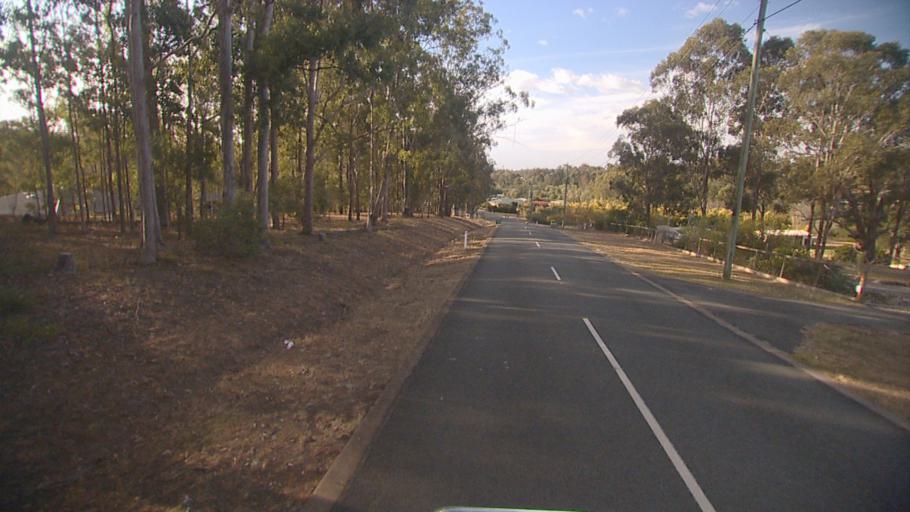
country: AU
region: Queensland
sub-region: Logan
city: Cedar Vale
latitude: -27.8831
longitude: 153.0099
